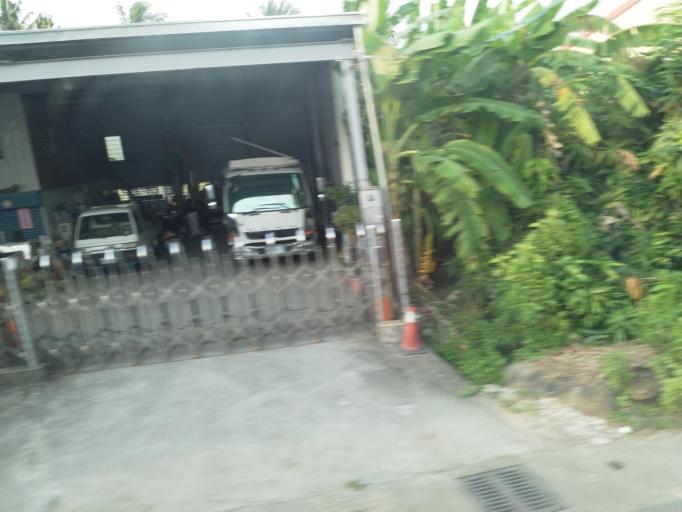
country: TW
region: Taiwan
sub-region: Pingtung
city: Pingtung
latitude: 22.8852
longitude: 120.5074
